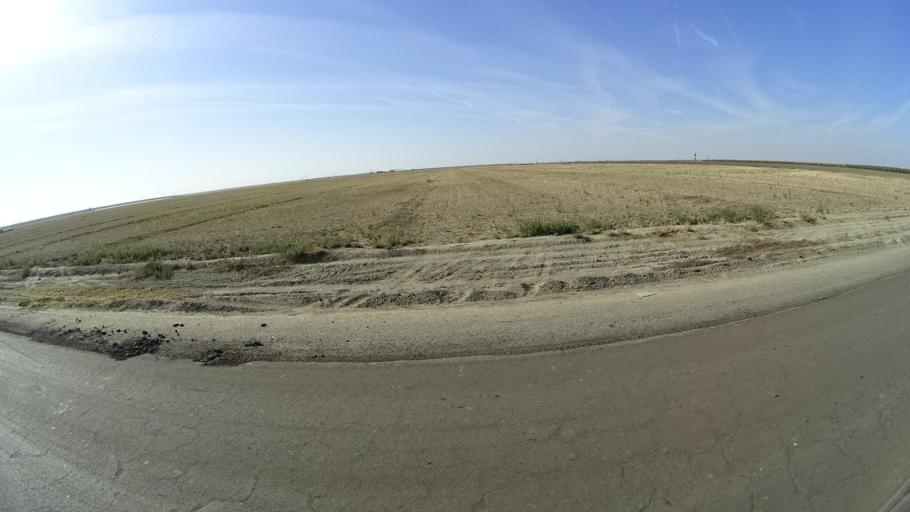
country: US
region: California
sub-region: Kern County
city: Wasco
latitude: 35.6696
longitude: -119.3840
